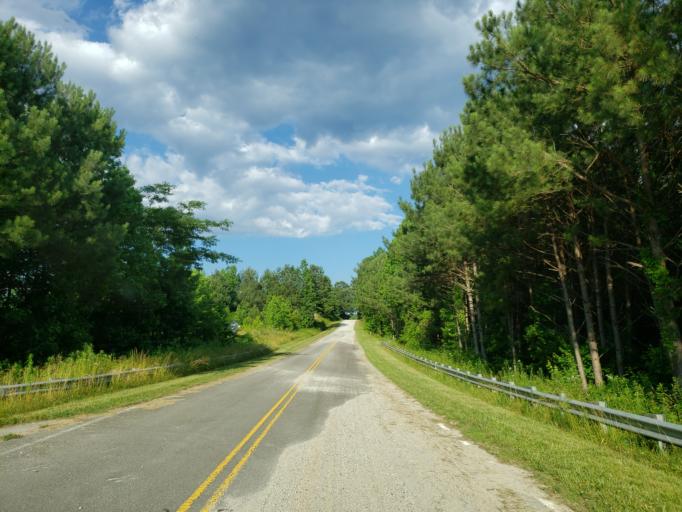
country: US
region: Georgia
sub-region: Haralson County
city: Buchanan
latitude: 33.8464
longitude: -85.2064
